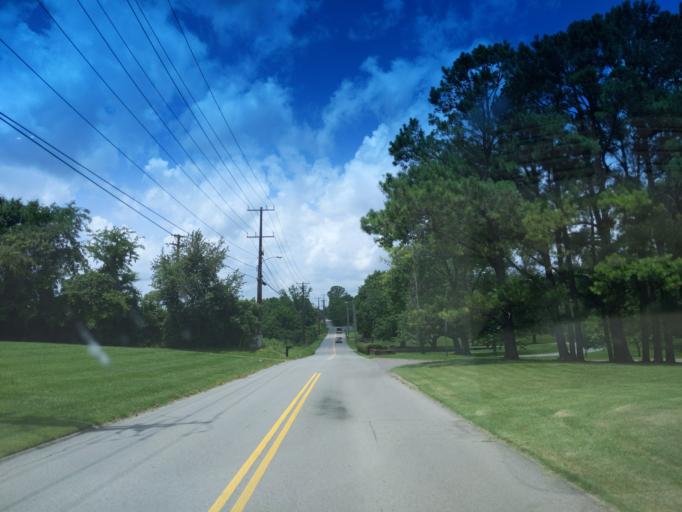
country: US
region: Tennessee
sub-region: Williamson County
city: Brentwood Estates
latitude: 36.0202
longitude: -86.7794
